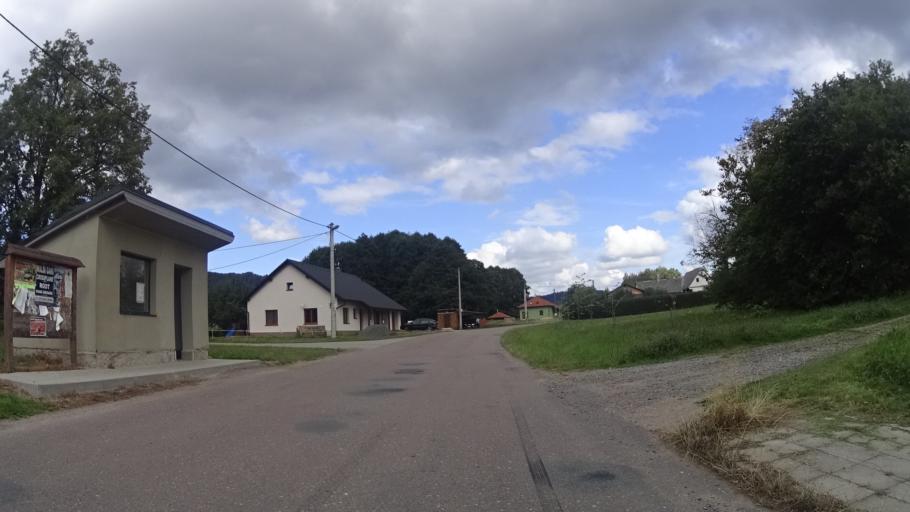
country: CZ
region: Pardubicky
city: Dolni Cermna
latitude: 49.9370
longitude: 16.5298
